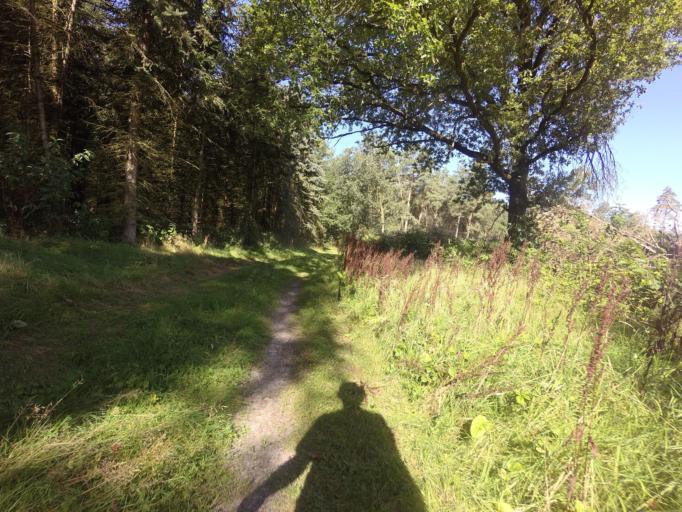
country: DE
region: Lower Saxony
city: Wielen
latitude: 52.5364
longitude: 6.7007
